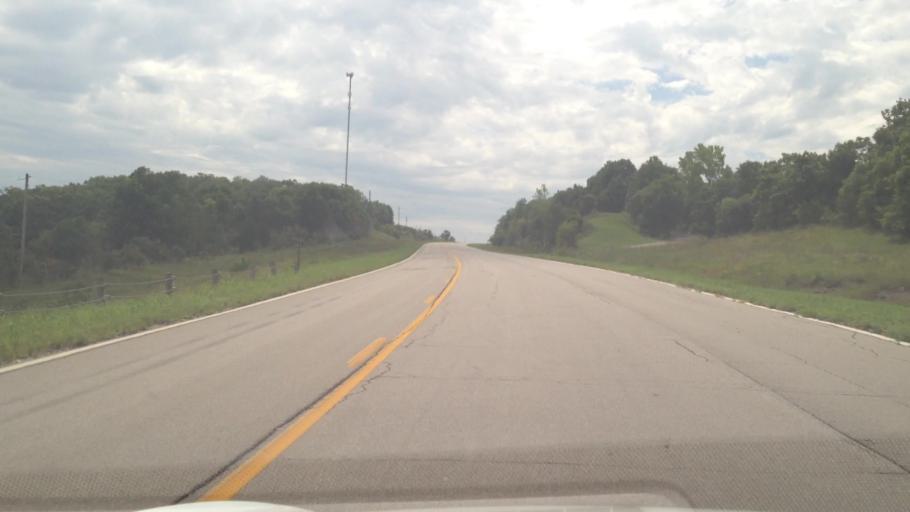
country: US
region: Kansas
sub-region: Bourbon County
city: Fort Scott
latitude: 37.8326
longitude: -94.9811
